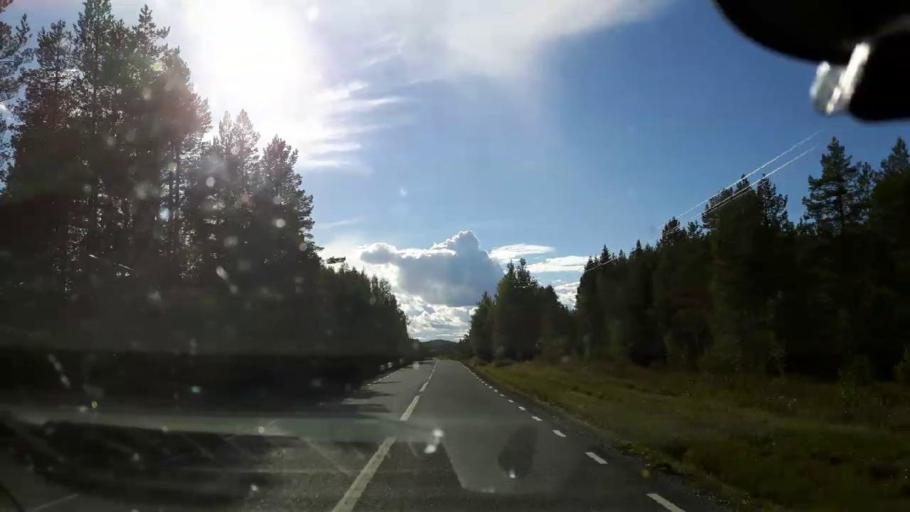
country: SE
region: Jaemtland
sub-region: Stroemsunds Kommun
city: Stroemsund
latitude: 63.5760
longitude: 15.6493
